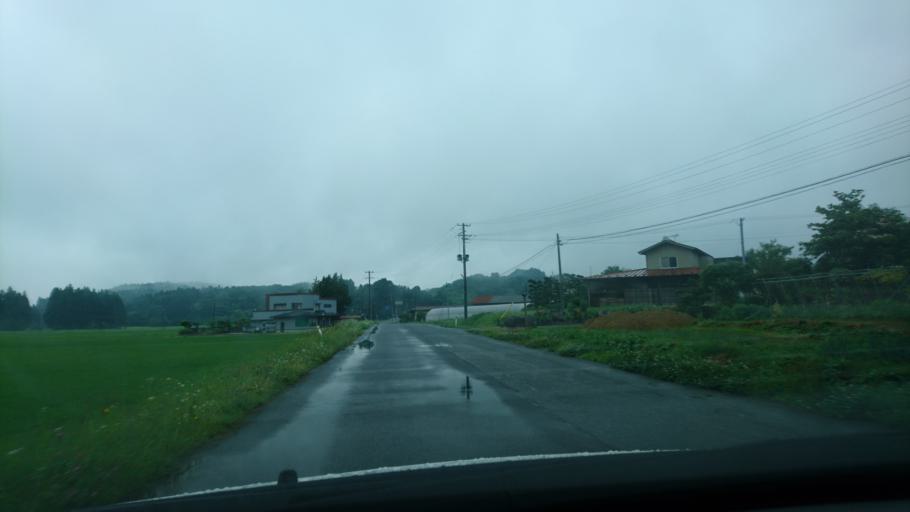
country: JP
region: Iwate
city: Ichinoseki
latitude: 38.8521
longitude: 141.0165
